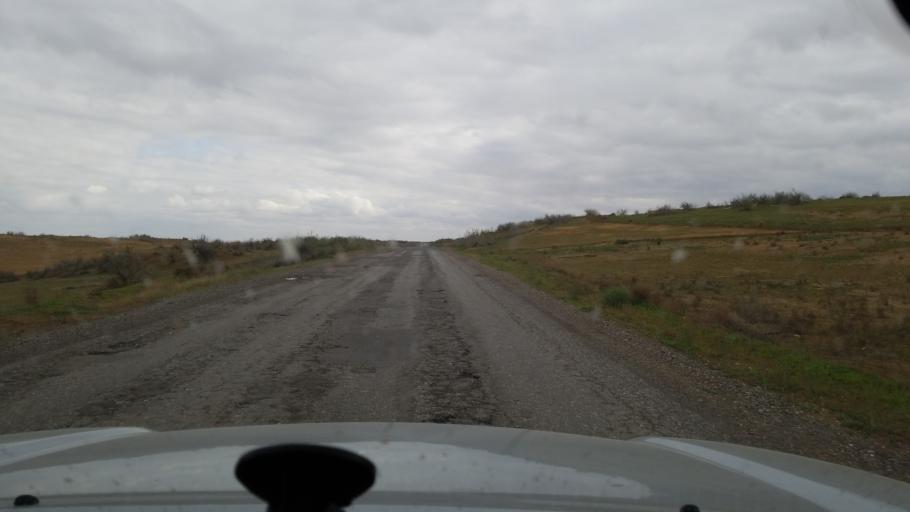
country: TM
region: Mary
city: Serhetabat
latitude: 36.0810
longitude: 62.6142
